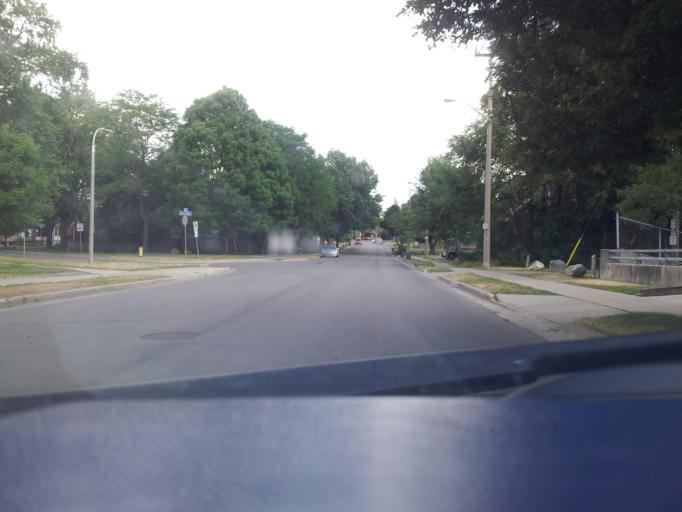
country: CA
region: Ontario
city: Kitchener
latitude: 43.4432
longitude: -80.5043
